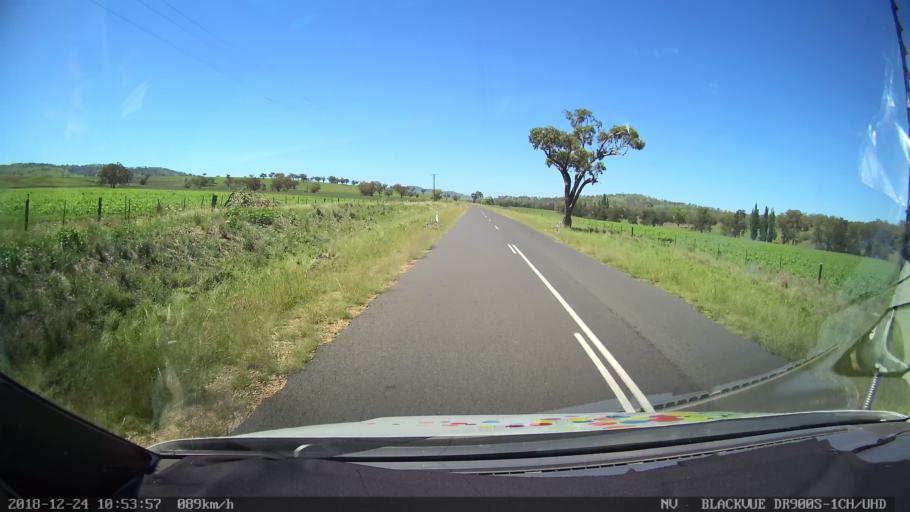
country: AU
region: New South Wales
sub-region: Upper Hunter Shire
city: Merriwa
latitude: -31.9976
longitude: 150.4189
